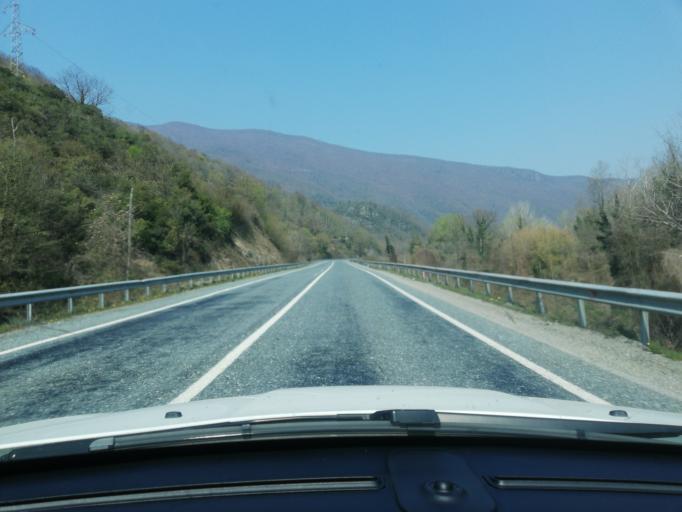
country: TR
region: Zonguldak
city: Gokcebey
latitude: 41.2557
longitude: 32.1605
